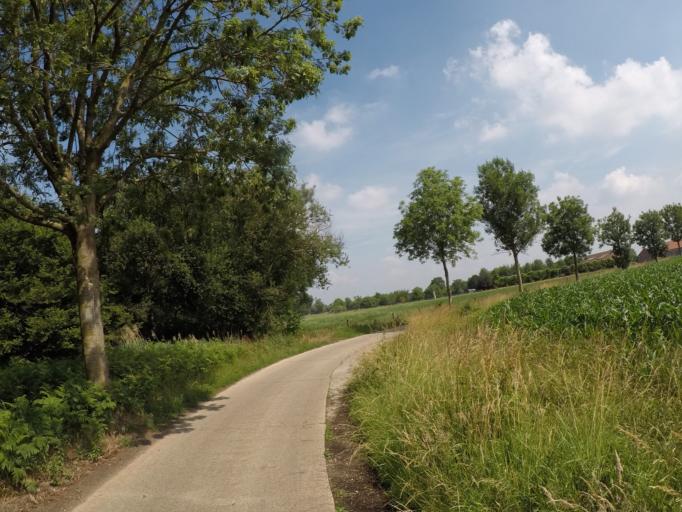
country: BE
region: Flanders
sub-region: Provincie Antwerpen
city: Brecht
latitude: 51.3547
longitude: 4.6106
